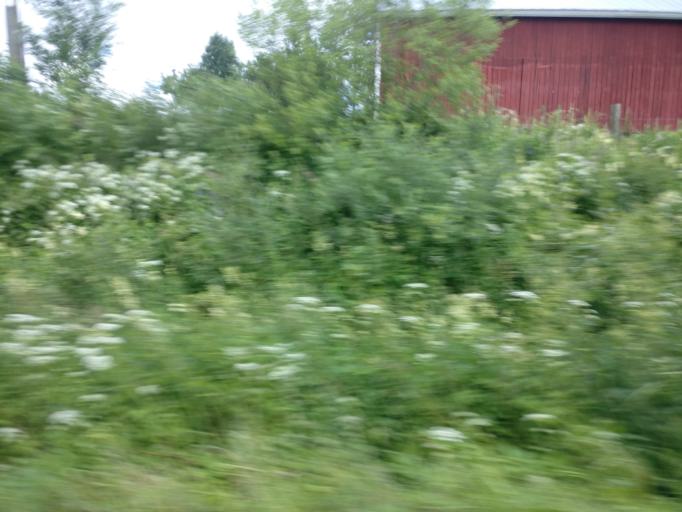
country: FI
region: Southern Savonia
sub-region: Savonlinna
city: Rantasalmi
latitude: 62.1397
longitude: 28.2347
